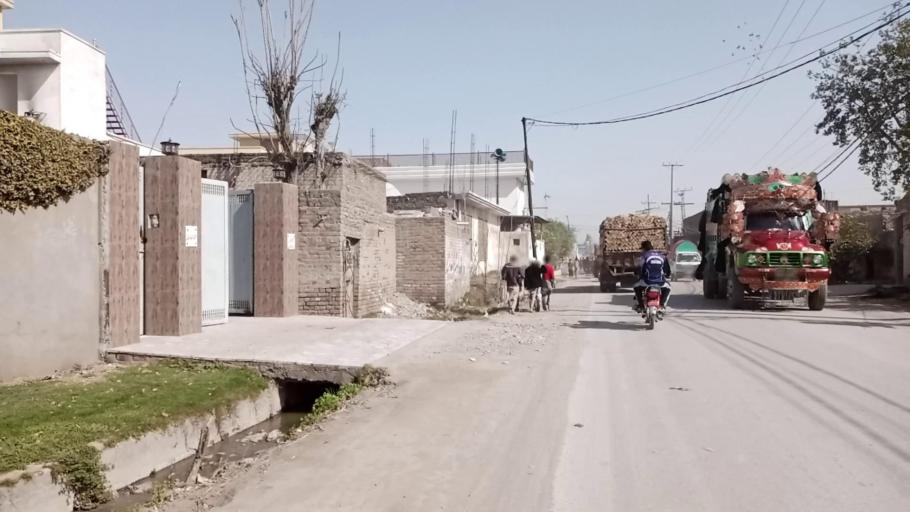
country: PK
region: Khyber Pakhtunkhwa
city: Peshawar
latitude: 34.0095
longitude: 71.6455
